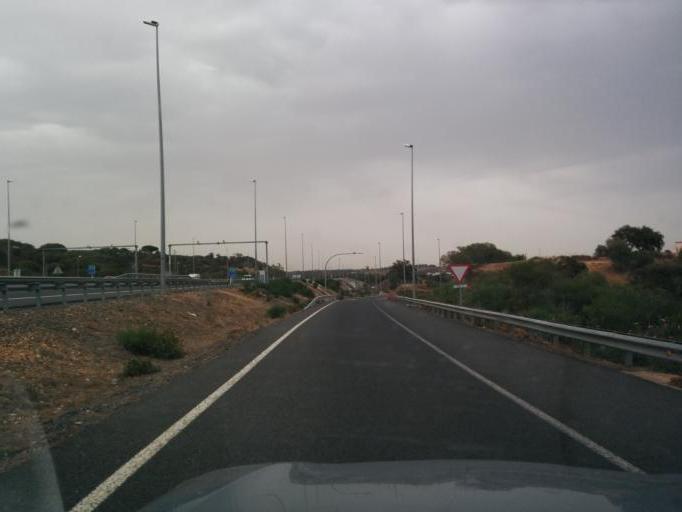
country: ES
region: Andalusia
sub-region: Provincia de Huelva
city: Ayamonte
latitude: 37.2389
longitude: -7.4077
